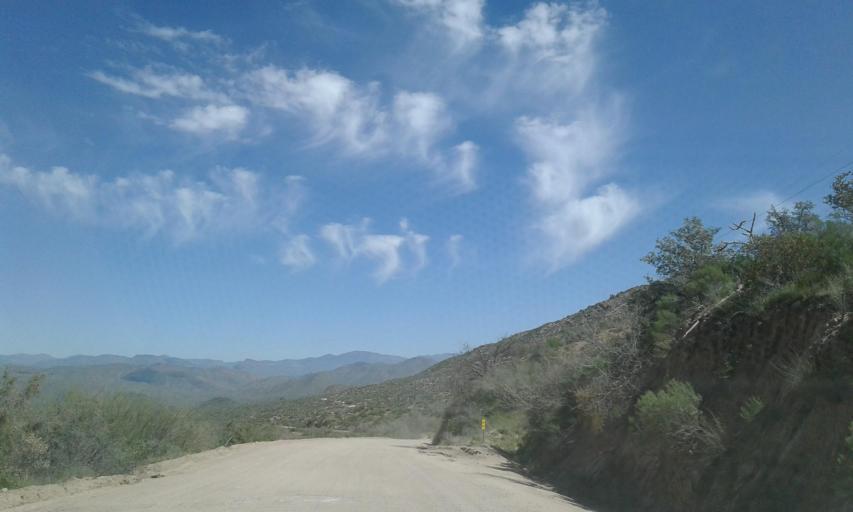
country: US
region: Arizona
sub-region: Pinal County
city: Gold Camp
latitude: 33.5479
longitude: -111.2565
